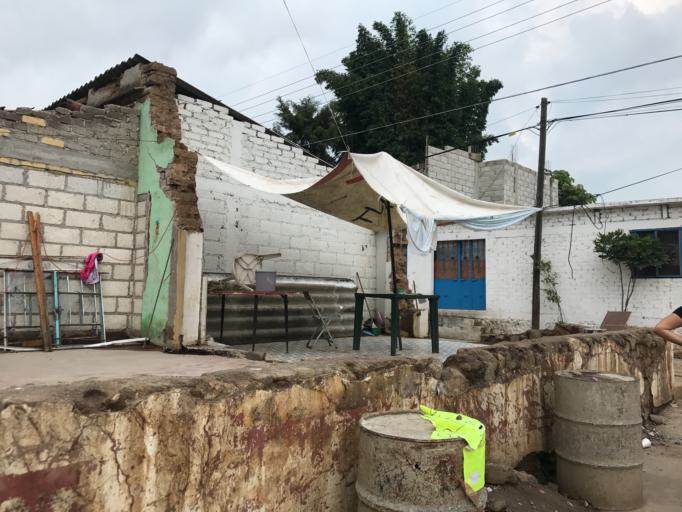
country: MX
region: Morelos
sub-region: Tlayacapan
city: Tlayacapan
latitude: 18.9613
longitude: -98.9832
